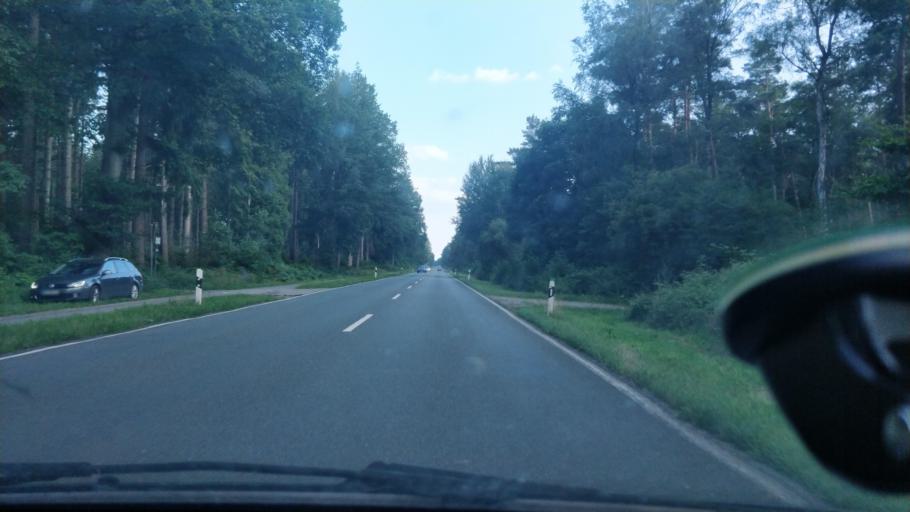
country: DE
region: North Rhine-Westphalia
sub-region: Regierungsbezirk Dusseldorf
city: Alpen
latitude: 51.5534
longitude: 6.5010
